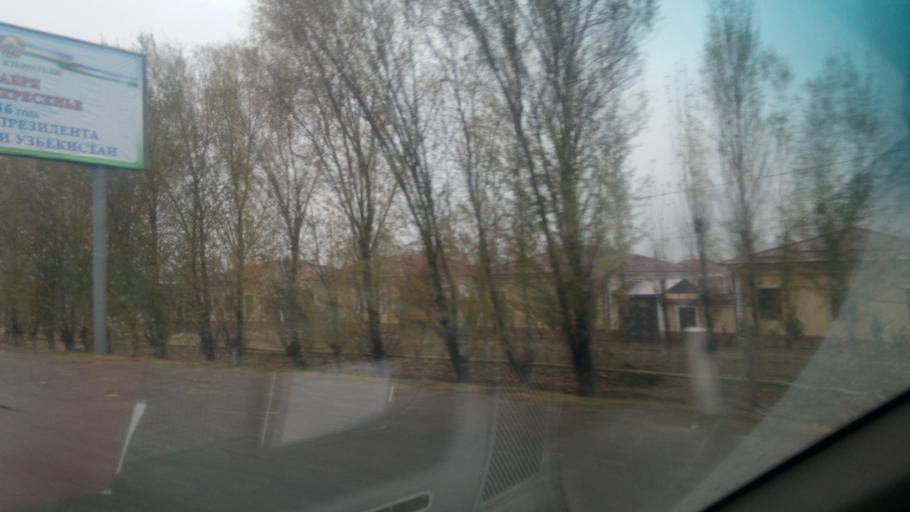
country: UZ
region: Toshkent
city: Urtaowul
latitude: 41.2243
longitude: 69.1418
